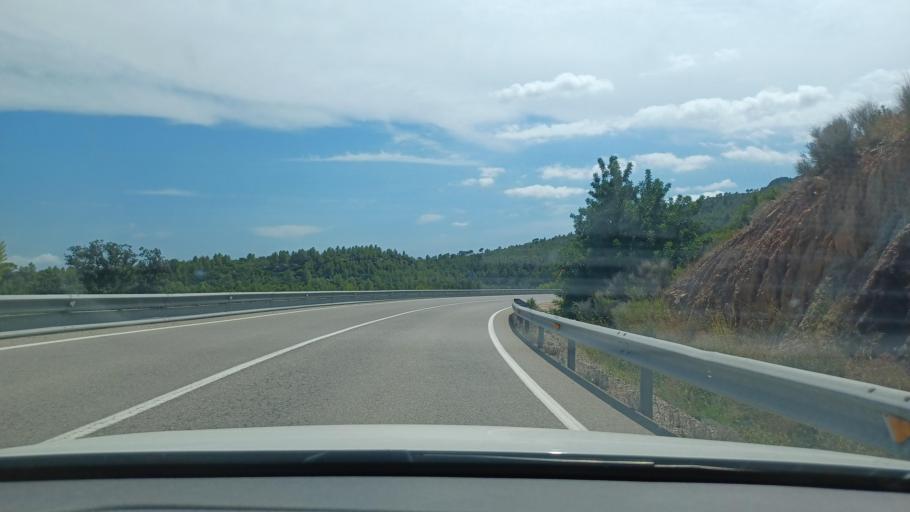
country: ES
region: Catalonia
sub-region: Provincia de Tarragona
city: Benifallet
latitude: 40.9469
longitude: 0.4609
